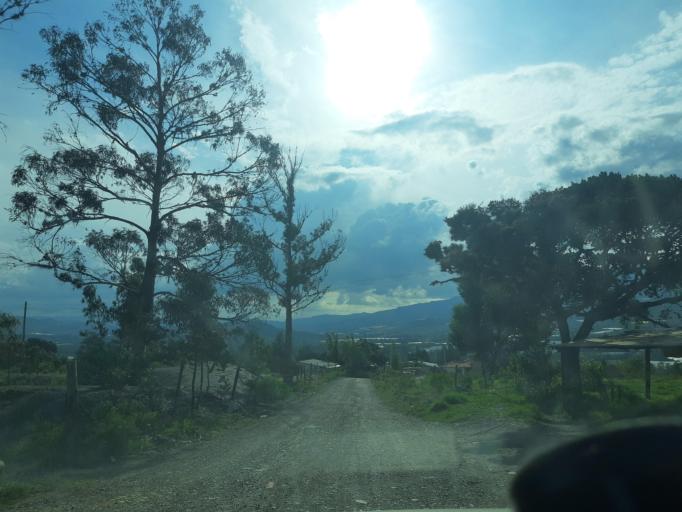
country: CO
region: Boyaca
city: Villa de Leiva
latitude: 5.6664
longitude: -73.5665
